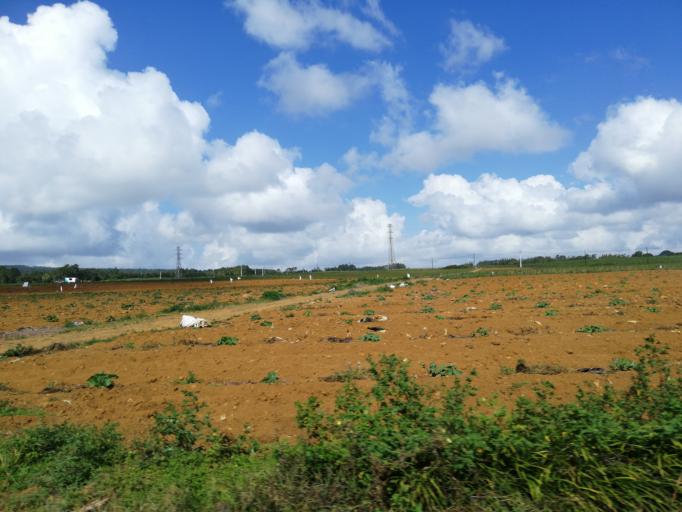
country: MU
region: Pamplemousses
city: Creve Coeur
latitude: -20.2095
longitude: 57.5571
